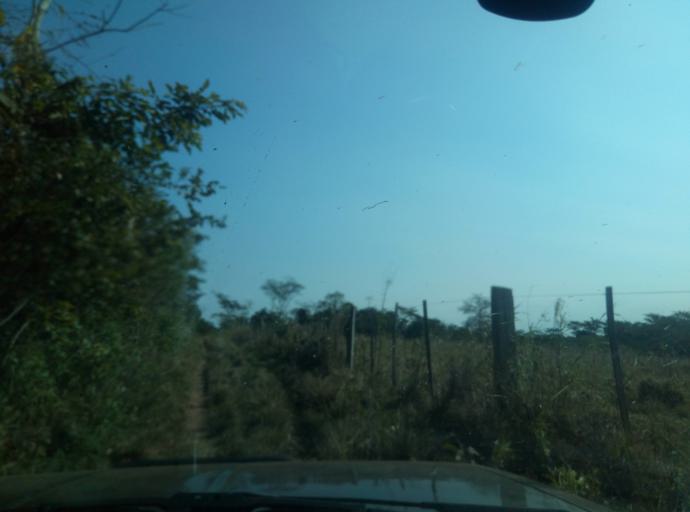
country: PY
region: Caaguazu
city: San Joaquin
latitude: -25.1574
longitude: -56.1290
